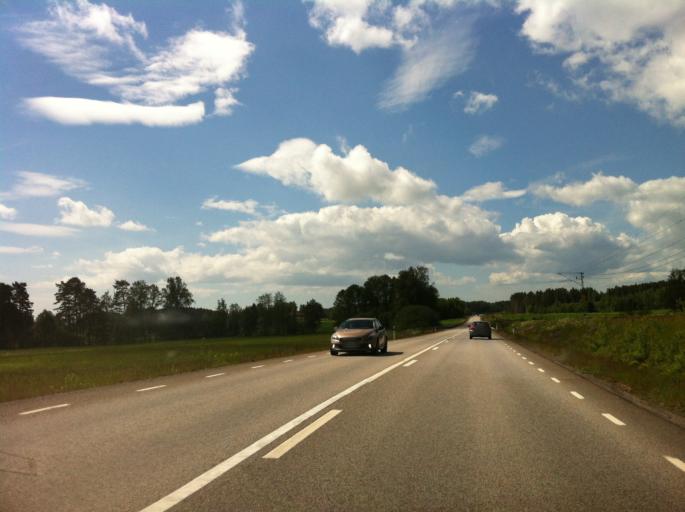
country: SE
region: Vaermland
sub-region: Saffle Kommun
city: Saeffle
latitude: 59.1654
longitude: 12.9989
